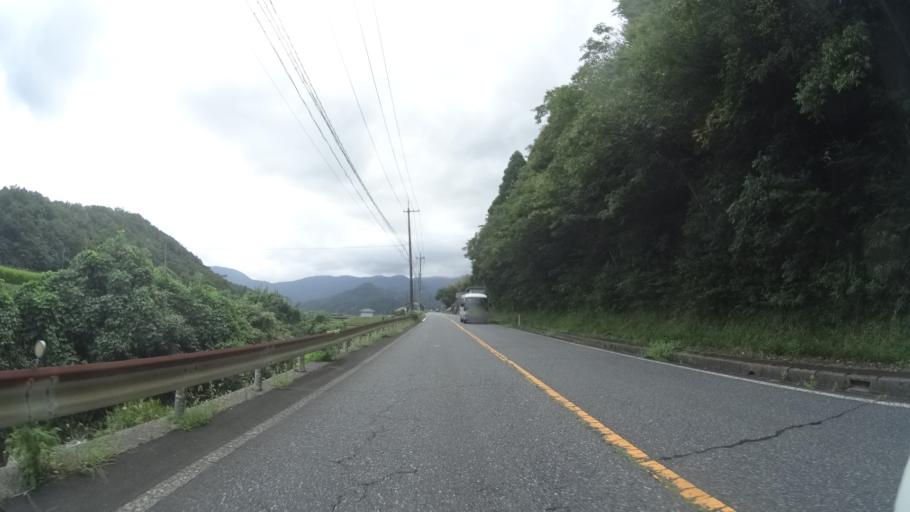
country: JP
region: Tottori
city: Tottori
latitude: 35.4714
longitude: 134.0763
